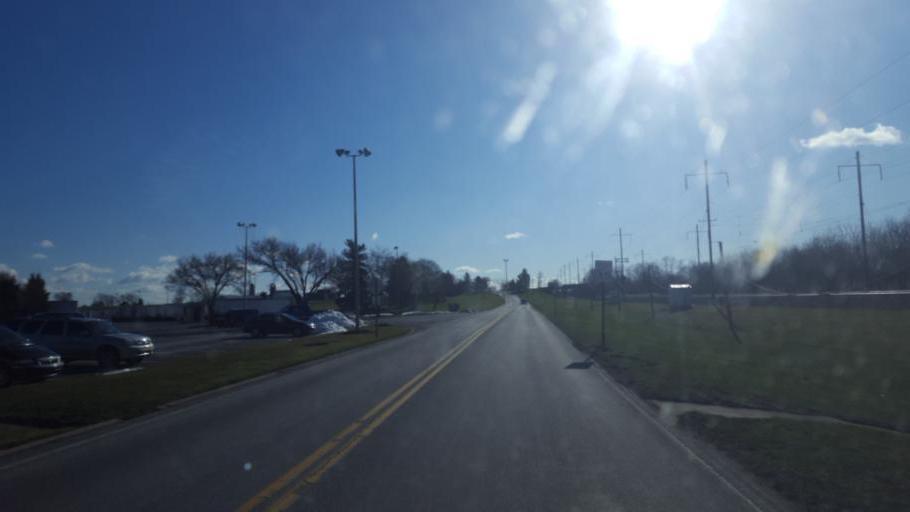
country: US
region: Pennsylvania
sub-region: Lancaster County
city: Lampeter
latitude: 40.0431
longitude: -76.2447
